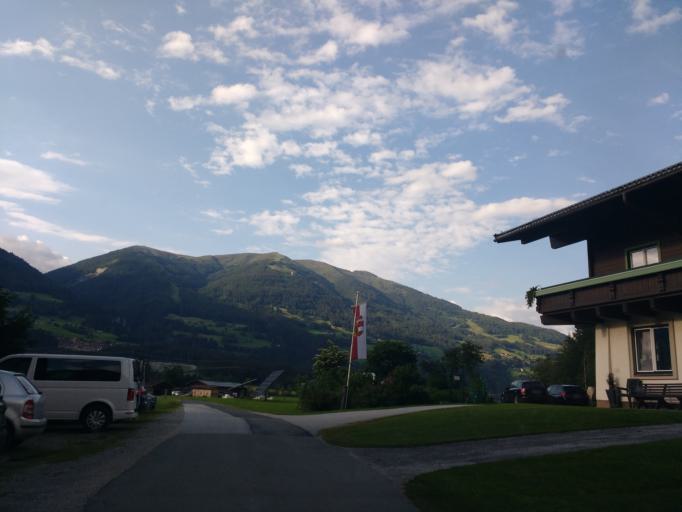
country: AT
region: Salzburg
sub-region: Politischer Bezirk Zell am See
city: Neukirchen am Grossvenediger
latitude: 47.2368
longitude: 12.2613
